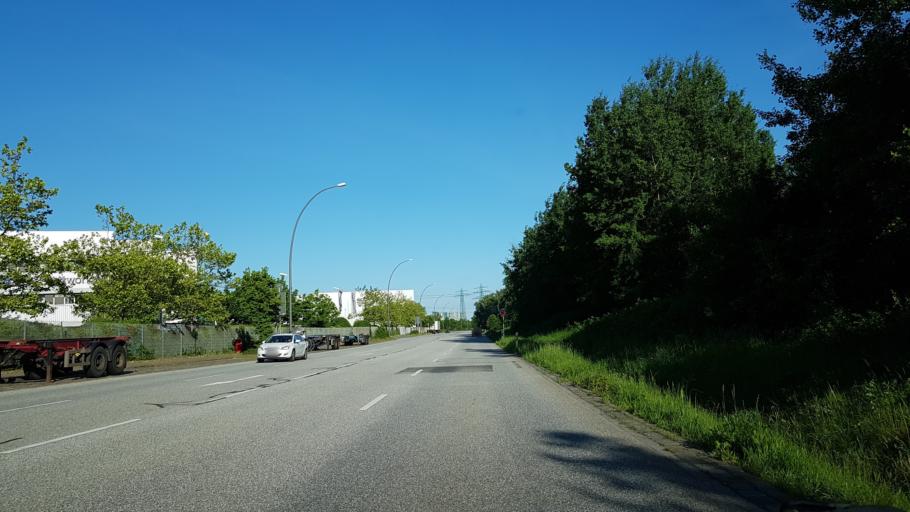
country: DE
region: Hamburg
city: Altona
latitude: 53.5044
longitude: 9.8983
